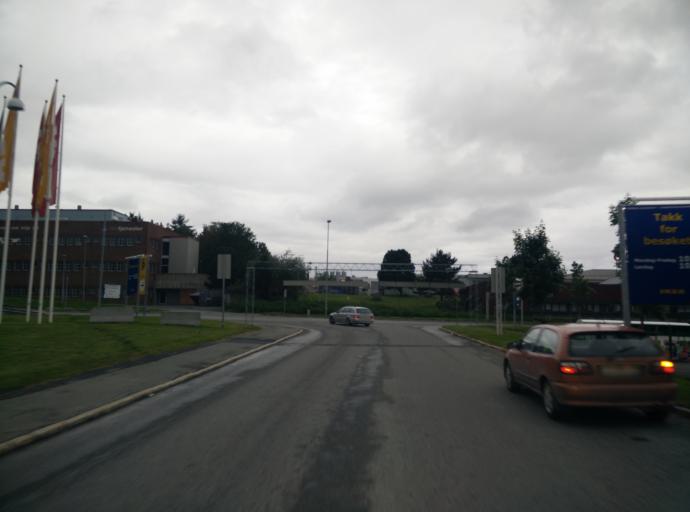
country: NO
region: Sor-Trondelag
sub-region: Trondheim
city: Trondheim
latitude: 63.4273
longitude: 10.4749
